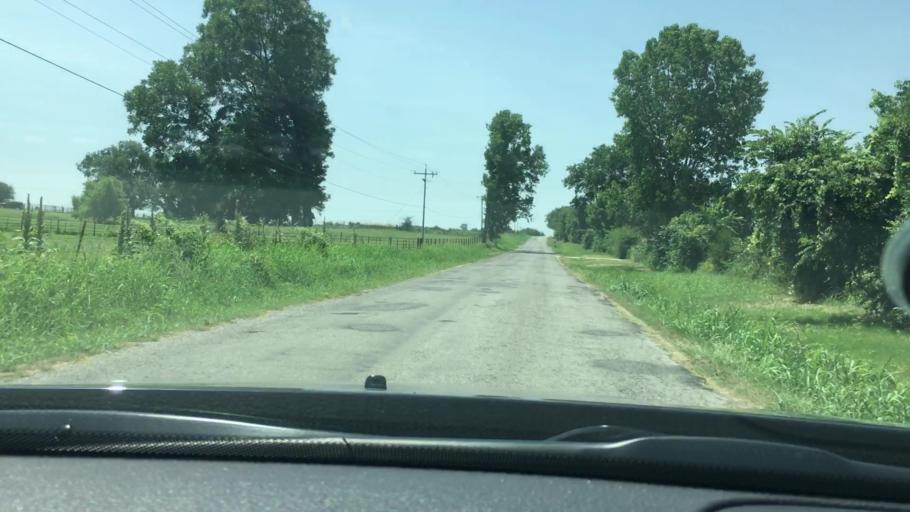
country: US
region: Oklahoma
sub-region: Pontotoc County
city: Byng
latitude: 34.8345
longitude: -96.6698
